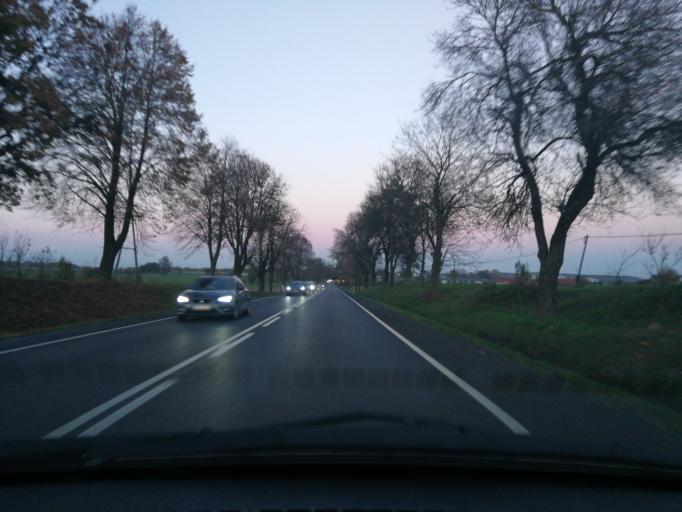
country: PL
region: Lodz Voivodeship
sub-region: Powiat lodzki wschodni
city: Andrespol
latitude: 51.8037
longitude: 19.6507
